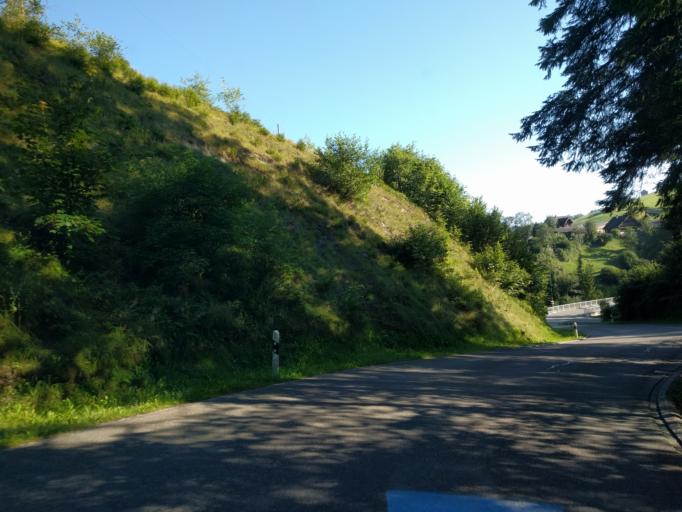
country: CH
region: Saint Gallen
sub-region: Wahlkreis Toggenburg
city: Sankt Peterzell
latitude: 47.2973
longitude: 9.1860
